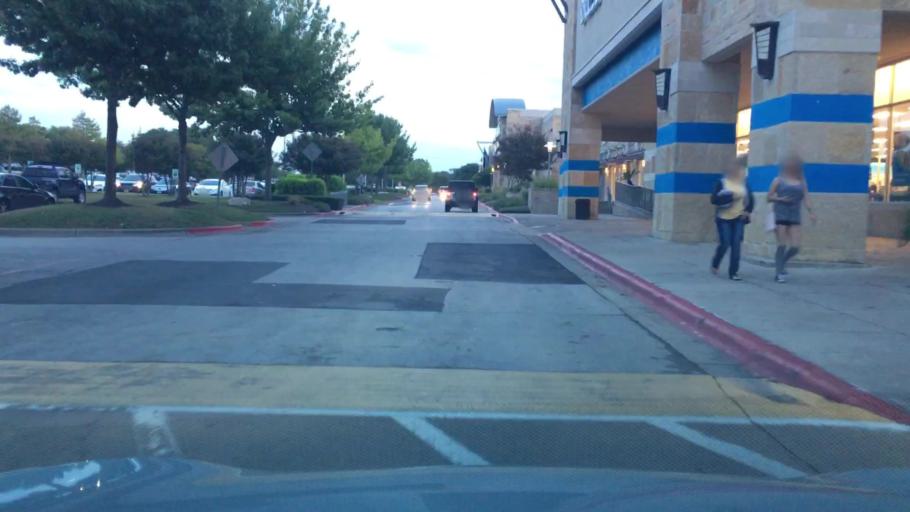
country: US
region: Texas
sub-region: Travis County
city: Onion Creek
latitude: 30.1603
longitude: -97.7936
